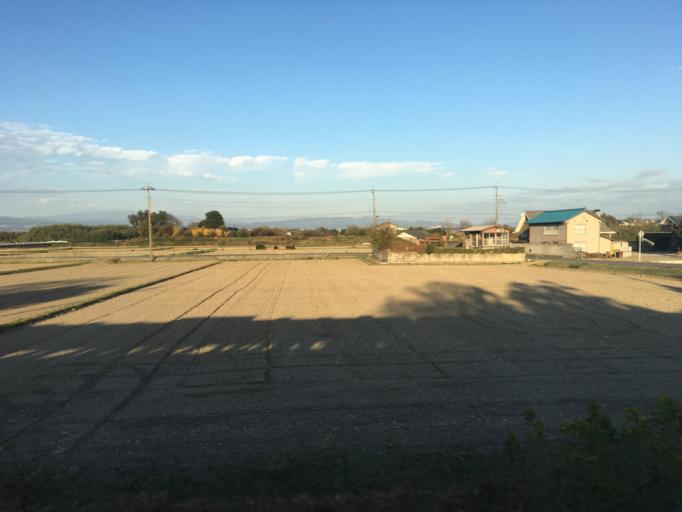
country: JP
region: Gunma
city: Isesaki
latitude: 36.3442
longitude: 139.1626
